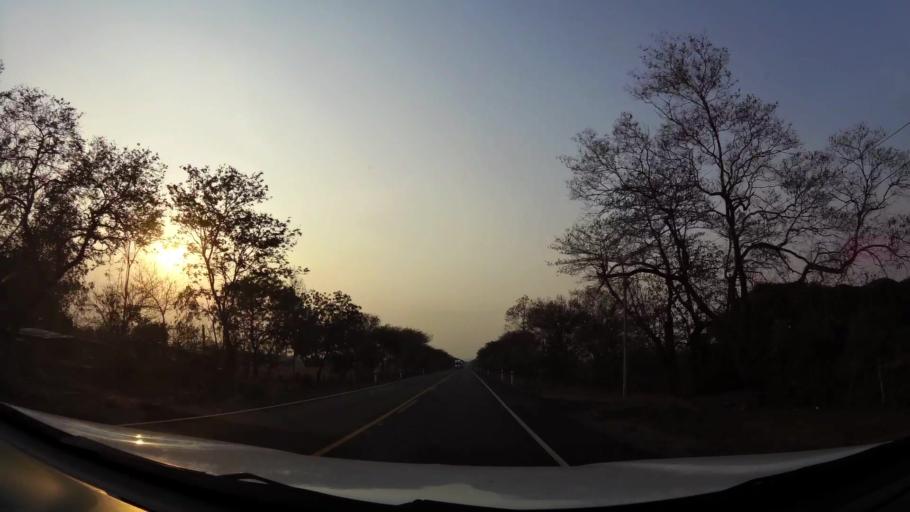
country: NI
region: Leon
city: Nagarote
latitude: 12.3017
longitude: -86.5970
